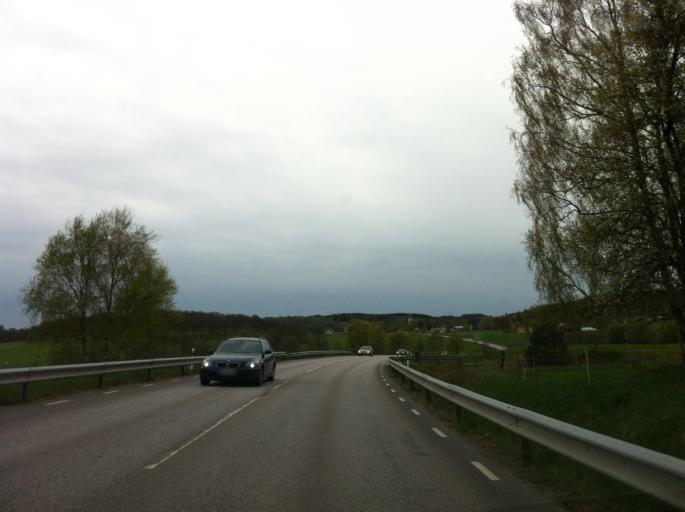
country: SE
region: Halland
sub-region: Falkenbergs Kommun
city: Falkenberg
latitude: 57.0713
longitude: 12.6601
